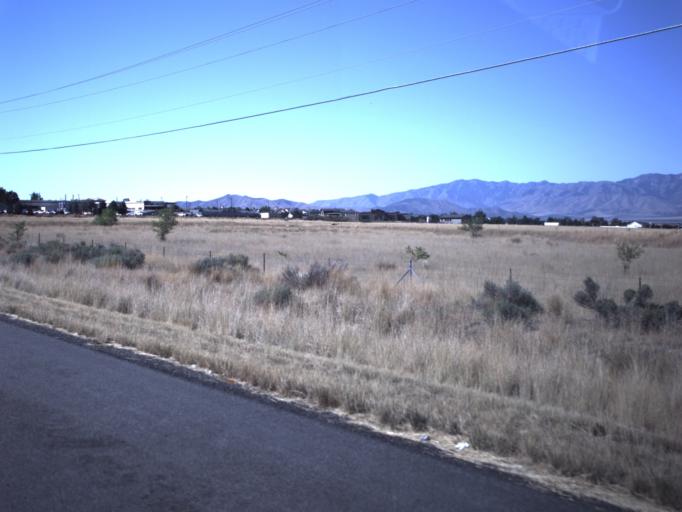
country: US
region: Utah
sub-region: Tooele County
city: Tooele
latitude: 40.5706
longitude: -112.2954
